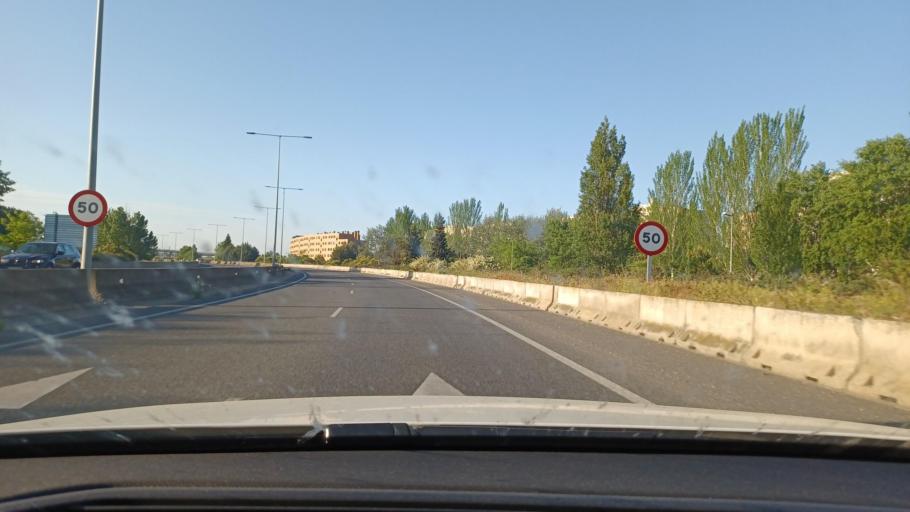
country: ES
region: Castille and Leon
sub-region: Provincia de Valladolid
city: Cisterniga
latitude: 41.6196
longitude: -4.7158
